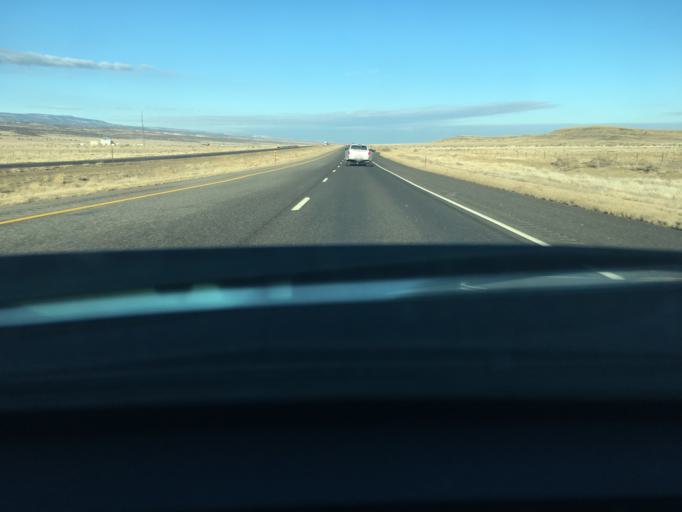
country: US
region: Colorado
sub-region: Mesa County
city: Palisade
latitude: 38.8677
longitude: -108.3313
